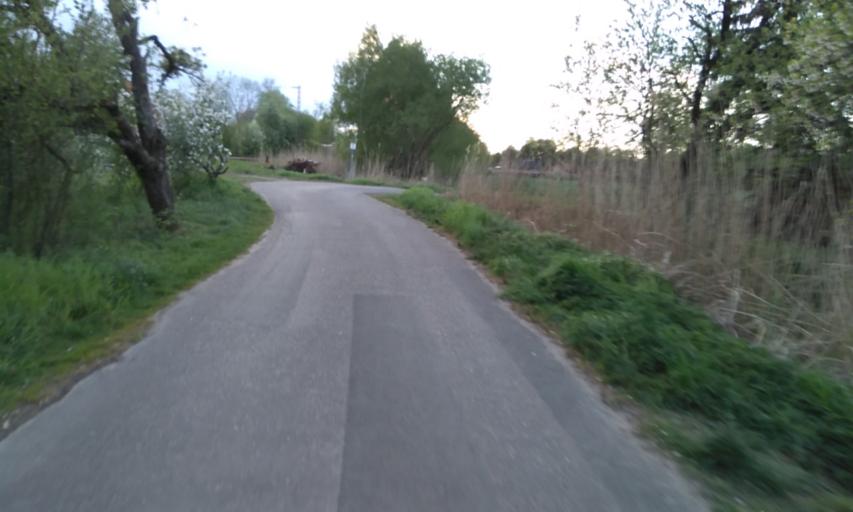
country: DE
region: Lower Saxony
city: Nottensdorf
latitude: 53.4999
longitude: 9.5937
